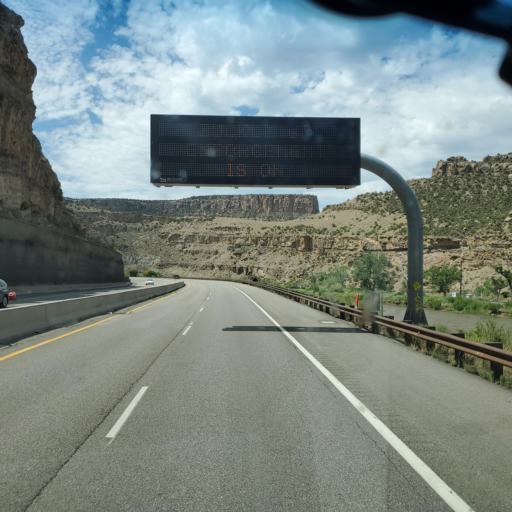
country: US
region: Colorado
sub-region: Mesa County
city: Palisade
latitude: 39.2022
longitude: -108.2669
